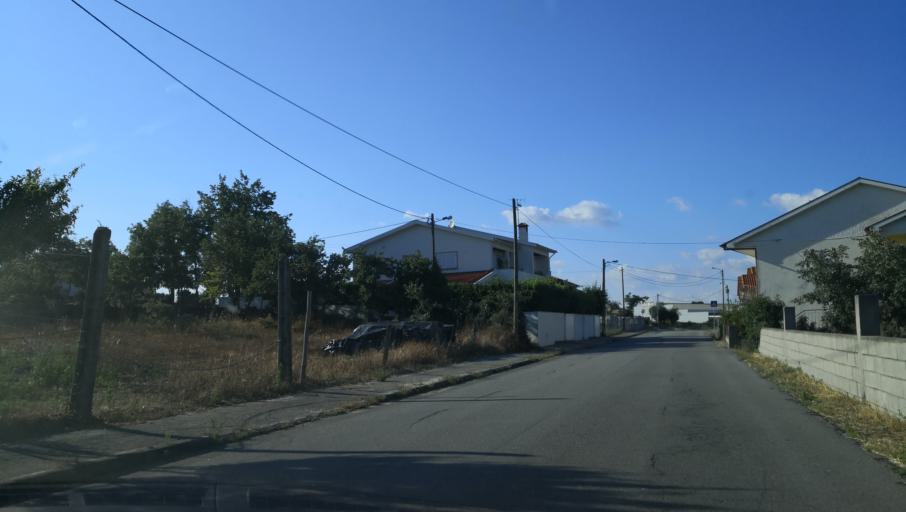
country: PT
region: Vila Real
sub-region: Chaves
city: Chaves
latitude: 41.7770
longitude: -7.4459
